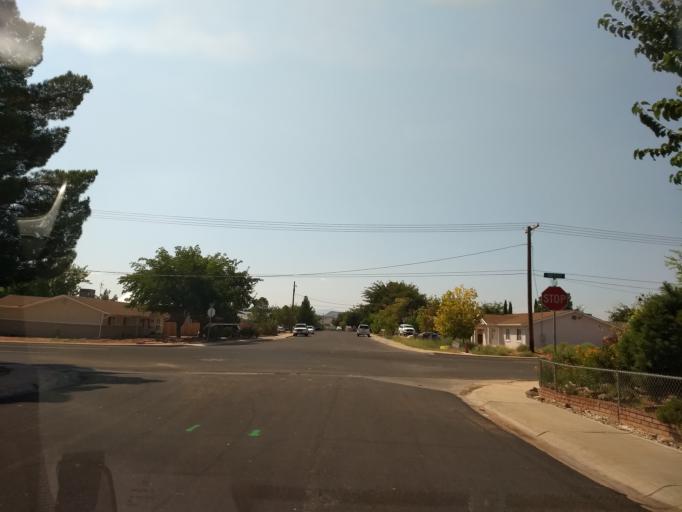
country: US
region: Utah
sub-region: Washington County
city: Washington
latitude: 37.1385
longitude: -113.5046
